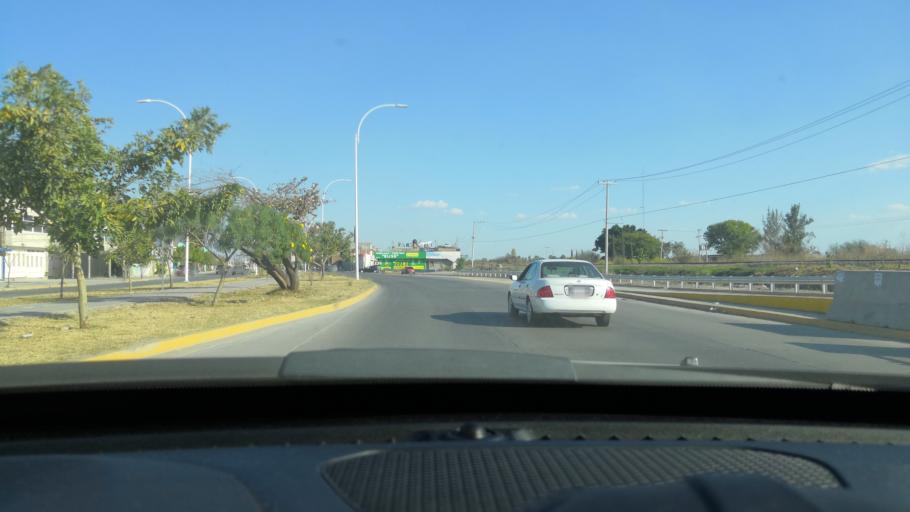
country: MX
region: Guanajuato
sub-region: Leon
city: San Jose de Duran (Los Troncoso)
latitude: 21.0654
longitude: -101.6332
